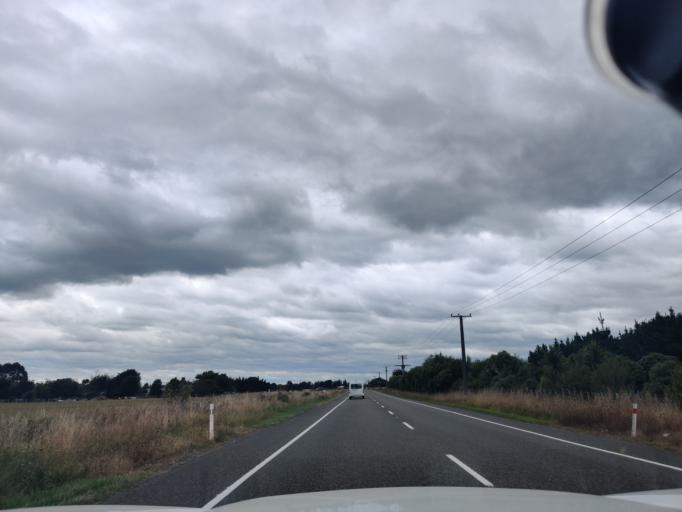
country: NZ
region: Manawatu-Wanganui
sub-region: Horowhenua District
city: Levin
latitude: -40.6493
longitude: 175.2869
